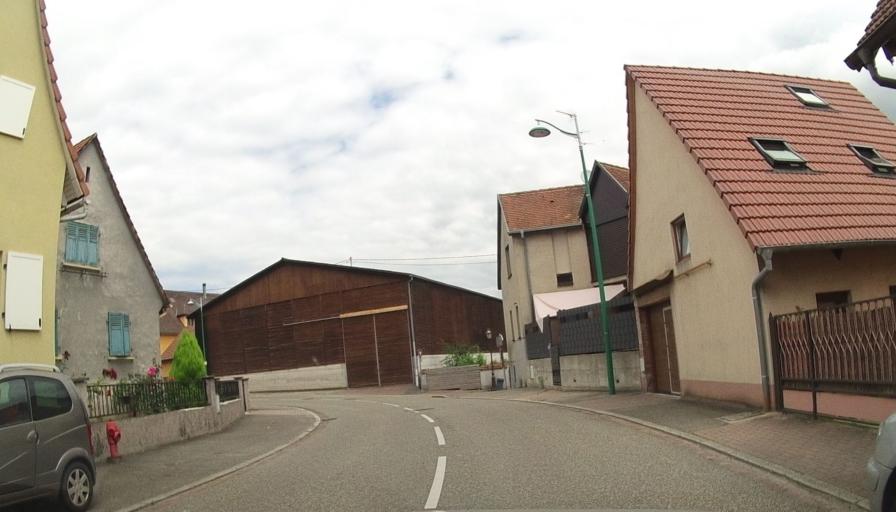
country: FR
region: Alsace
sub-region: Departement du Bas-Rhin
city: Seltz
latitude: 48.8944
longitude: 8.1090
